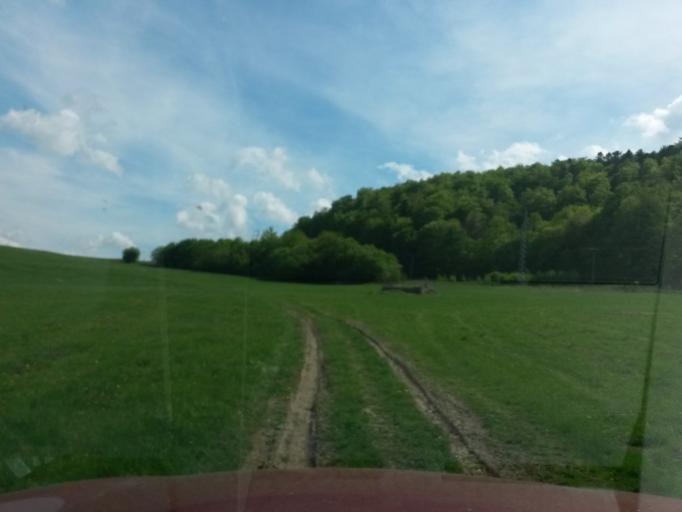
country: SK
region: Kosicky
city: Gelnica
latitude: 48.8316
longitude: 21.0568
